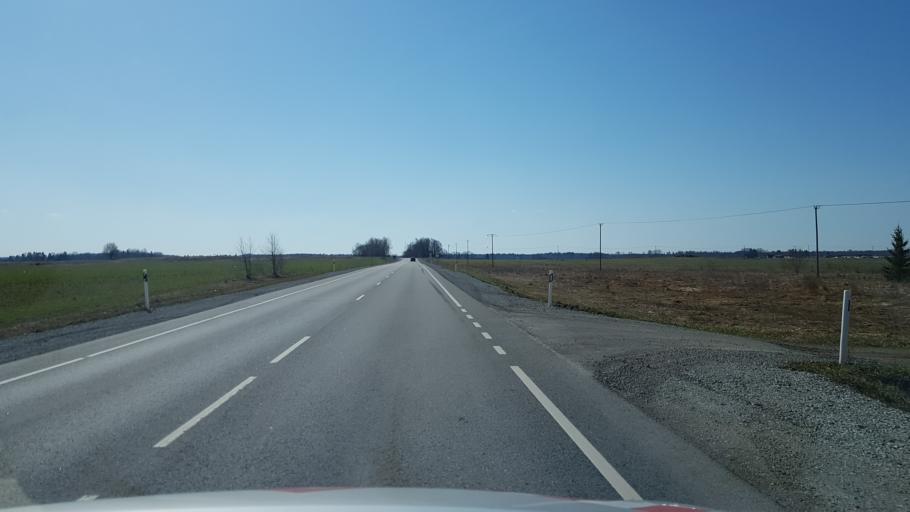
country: EE
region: Ida-Virumaa
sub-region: Kohtla-Jaerve linn
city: Kohtla-Jarve
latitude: 59.3540
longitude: 27.2402
